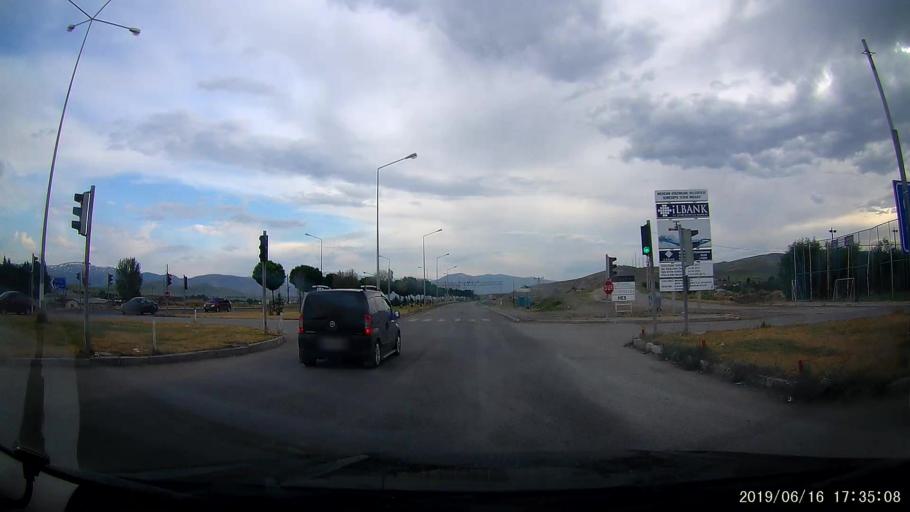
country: TR
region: Erzincan
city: Tercan
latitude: 39.7386
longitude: 40.2655
